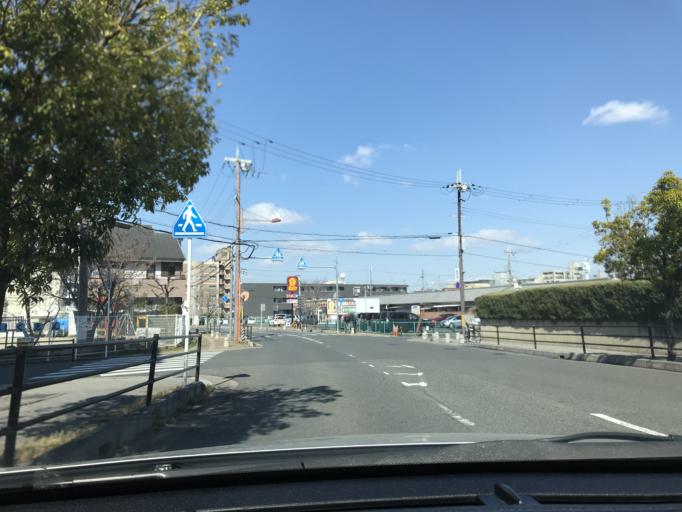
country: JP
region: Nara
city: Nara-shi
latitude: 34.6793
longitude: 135.8164
